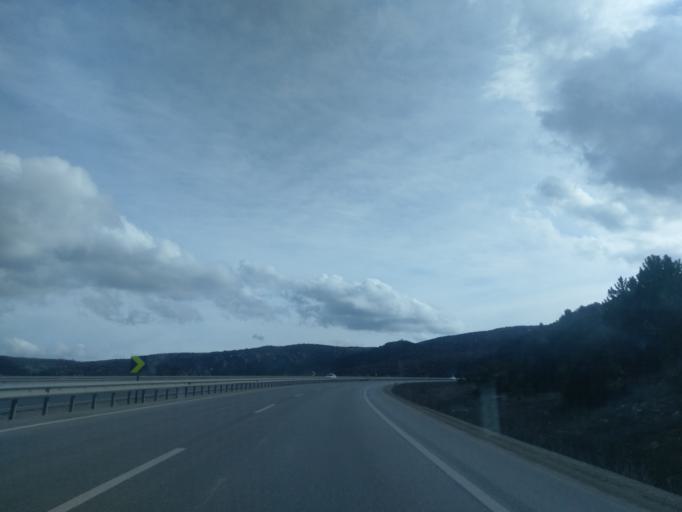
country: TR
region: Kuetahya
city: Sabuncu
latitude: 39.5622
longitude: 30.0761
